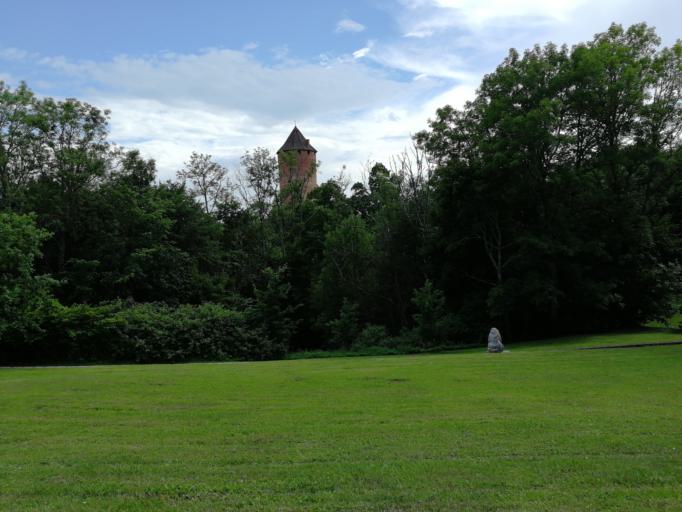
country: LV
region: Sigulda
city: Sigulda
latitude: 57.1844
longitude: 24.8505
